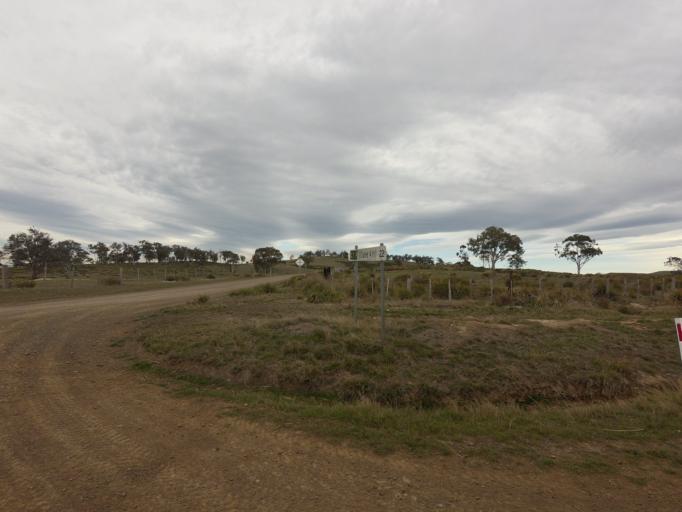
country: AU
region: Tasmania
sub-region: Derwent Valley
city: New Norfolk
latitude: -42.3899
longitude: 146.8841
